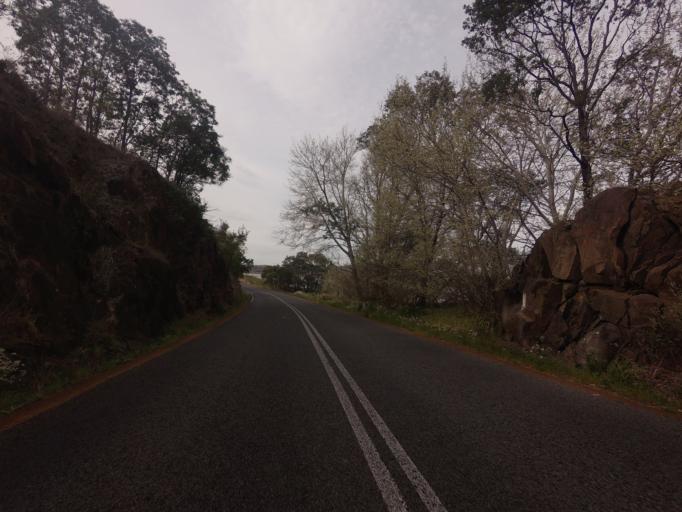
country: AU
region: Tasmania
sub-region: Sorell
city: Sorell
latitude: -42.4908
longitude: 147.9332
